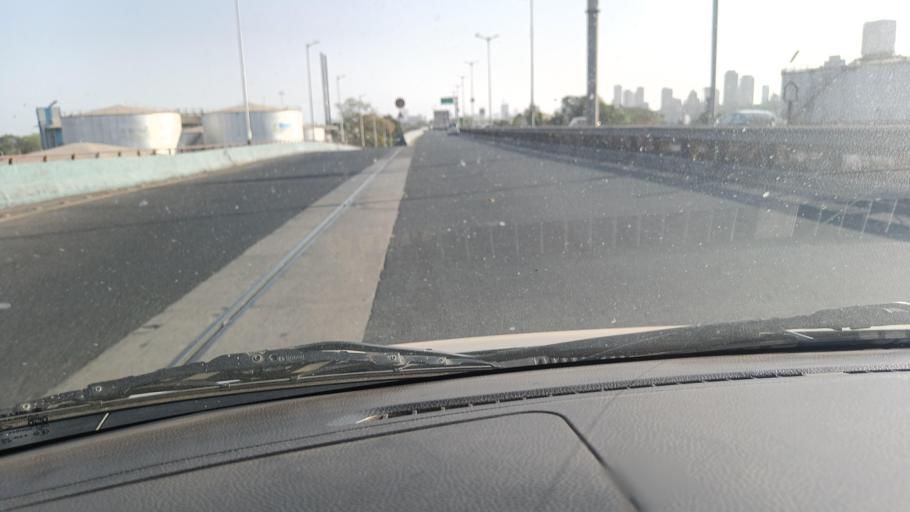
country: IN
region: Maharashtra
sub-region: Mumbai Suburban
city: Mumbai
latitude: 18.9635
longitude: 72.8452
